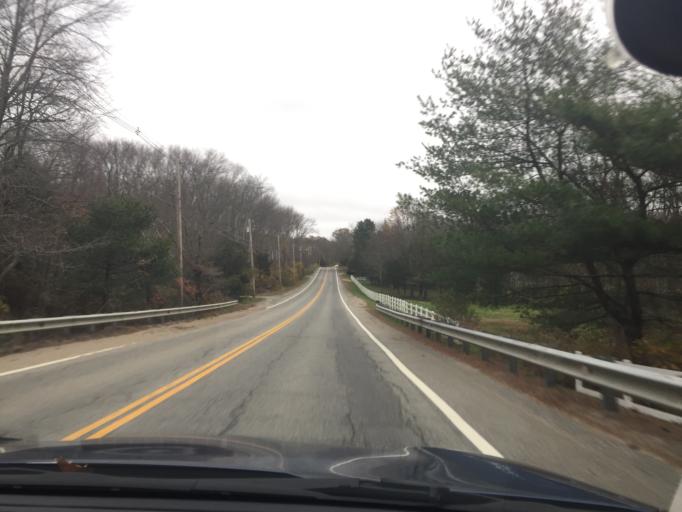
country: US
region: Rhode Island
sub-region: Providence County
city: North Scituate
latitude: 41.7918
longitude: -71.6225
